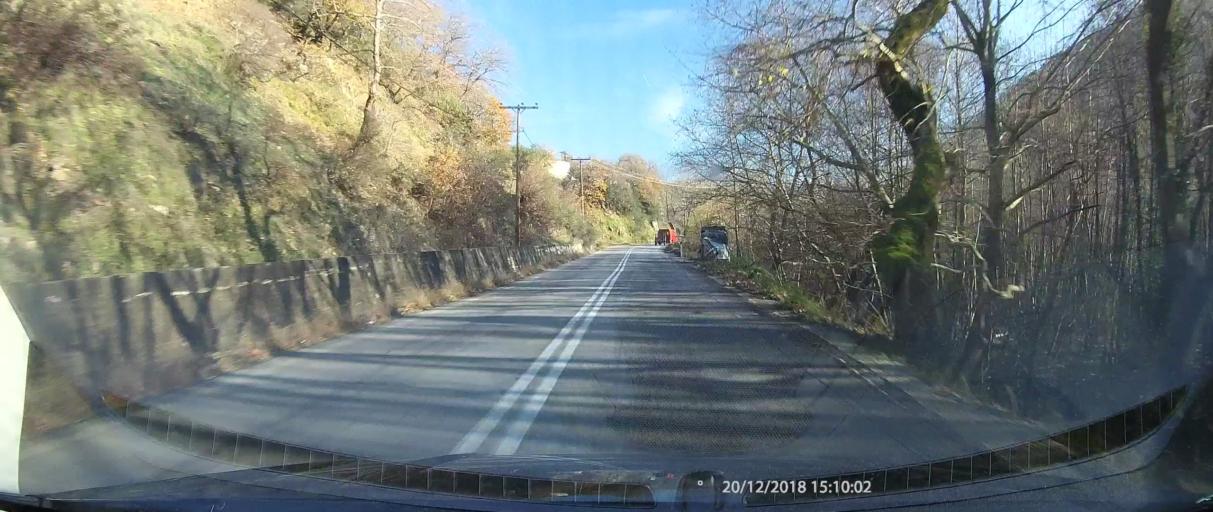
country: GR
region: Central Greece
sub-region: Nomos Fthiotidos
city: Makrakomi
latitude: 38.9487
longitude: 21.9486
